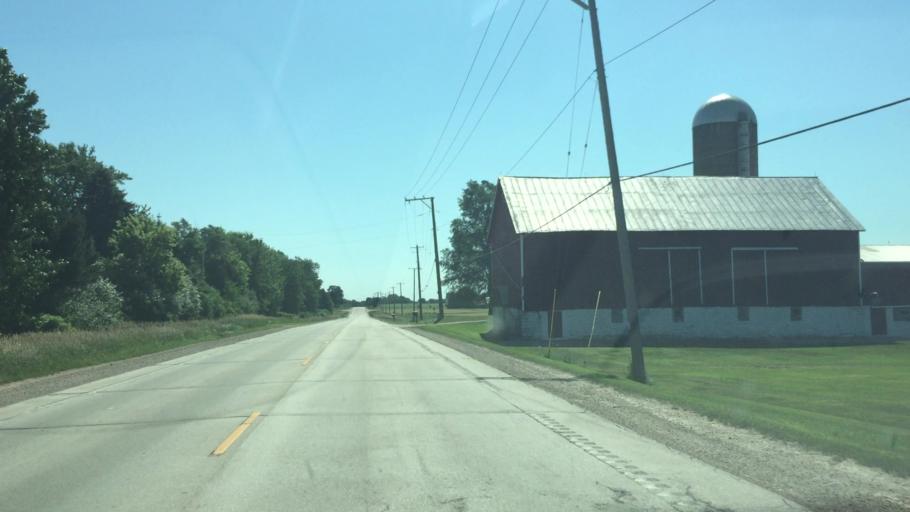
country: US
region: Wisconsin
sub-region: Calumet County
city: Hilbert
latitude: 44.1402
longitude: -88.1923
